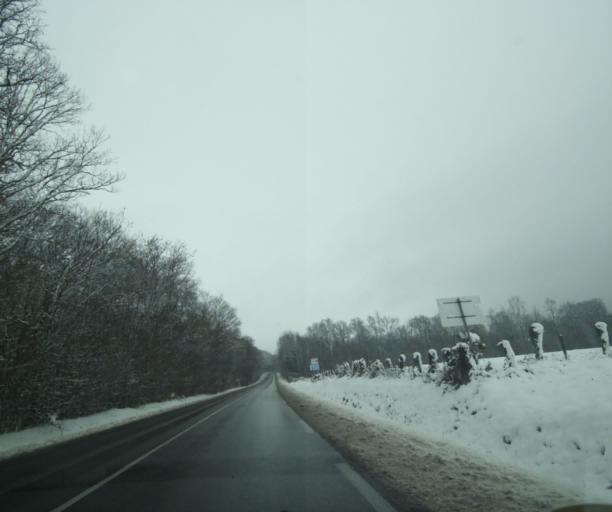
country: FR
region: Champagne-Ardenne
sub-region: Departement de la Haute-Marne
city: Montier-en-Der
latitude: 48.4869
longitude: 4.7752
